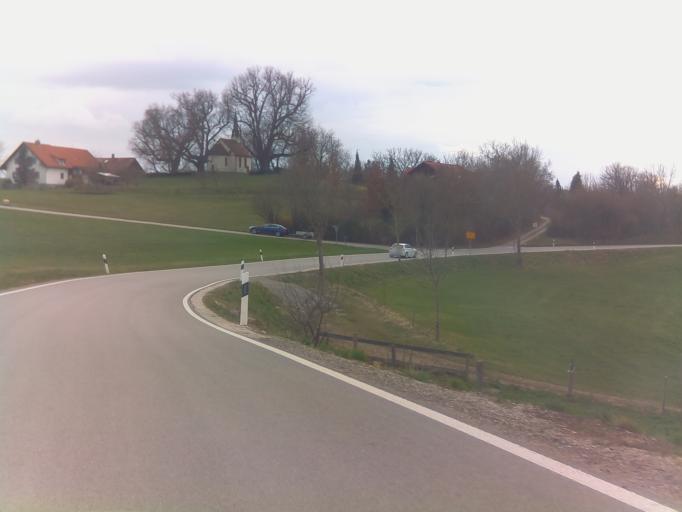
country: DE
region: Bavaria
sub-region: Upper Bavaria
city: Windach
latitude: 48.0275
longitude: 11.0188
